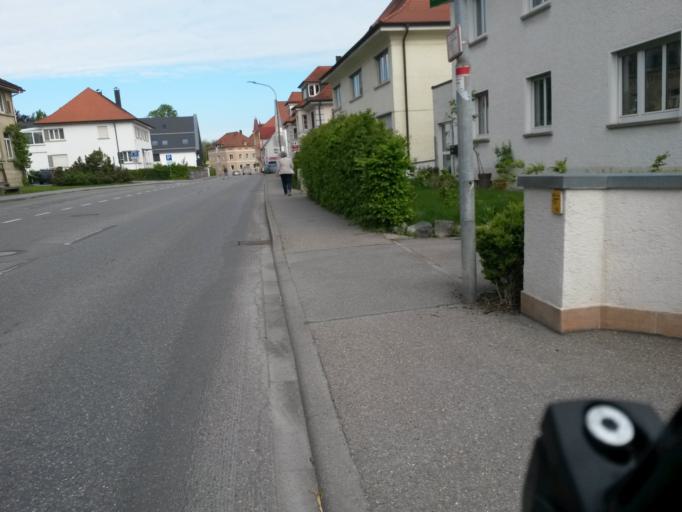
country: DE
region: Baden-Wuerttemberg
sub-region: Tuebingen Region
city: Bad Waldsee
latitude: 47.9181
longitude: 9.7573
